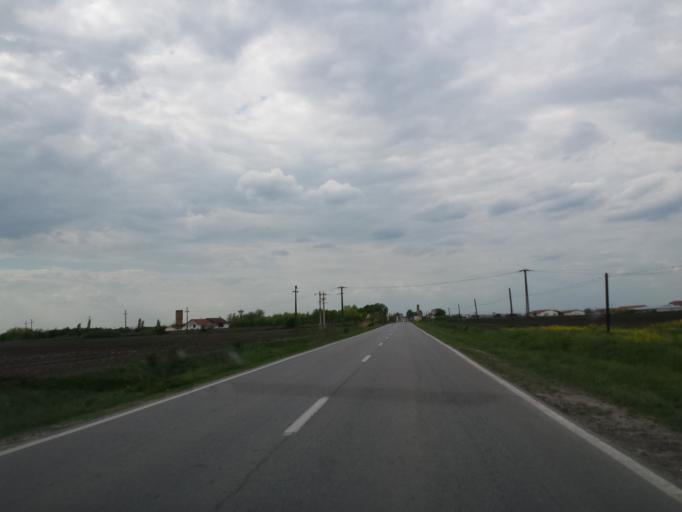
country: RO
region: Timis
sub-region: Comuna Sanpetru Mare
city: Sanpetru Mare
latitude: 46.0472
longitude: 20.6495
